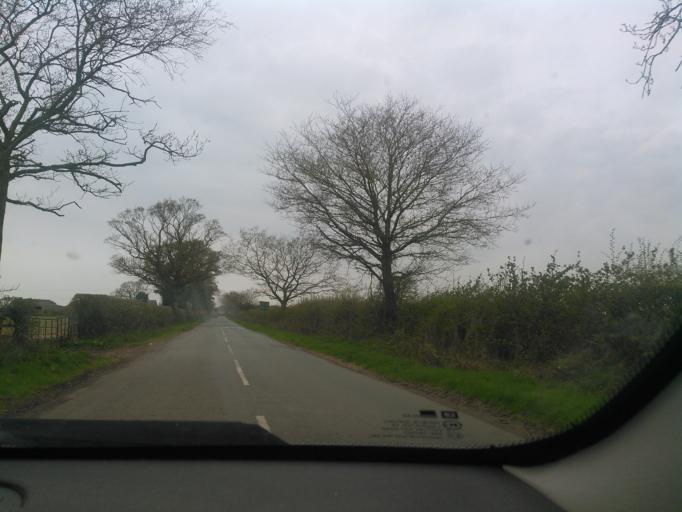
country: GB
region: England
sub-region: Shropshire
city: Shawbury
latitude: 52.8062
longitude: -2.6114
